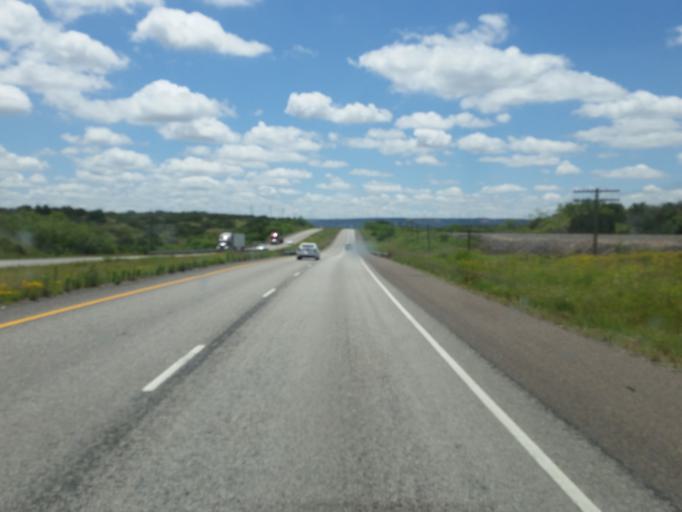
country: US
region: Texas
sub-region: Garza County
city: Post
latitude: 33.0256
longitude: -101.1842
